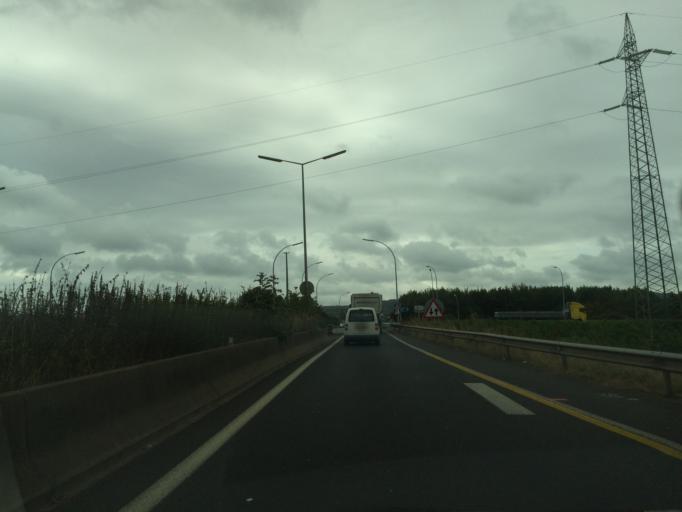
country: LU
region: Luxembourg
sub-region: Canton d'Esch-sur-Alzette
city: Esch-sur-Alzette
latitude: 49.5139
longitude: 5.9756
